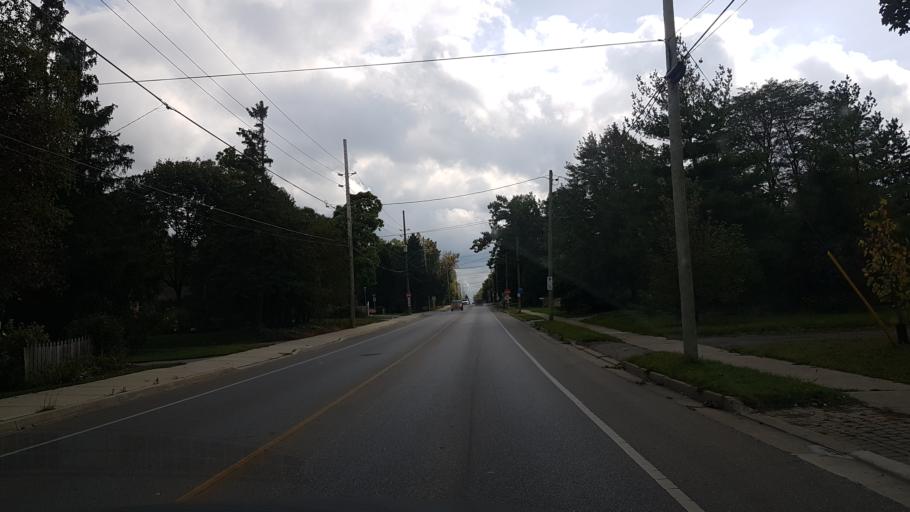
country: CA
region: Ontario
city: London
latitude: 42.9541
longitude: -81.2410
